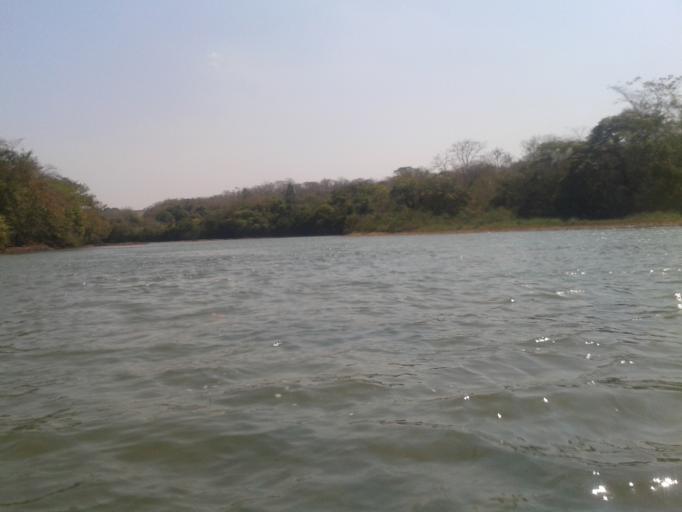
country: BR
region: Minas Gerais
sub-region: Ituiutaba
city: Ituiutaba
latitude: -18.9468
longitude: -49.4375
